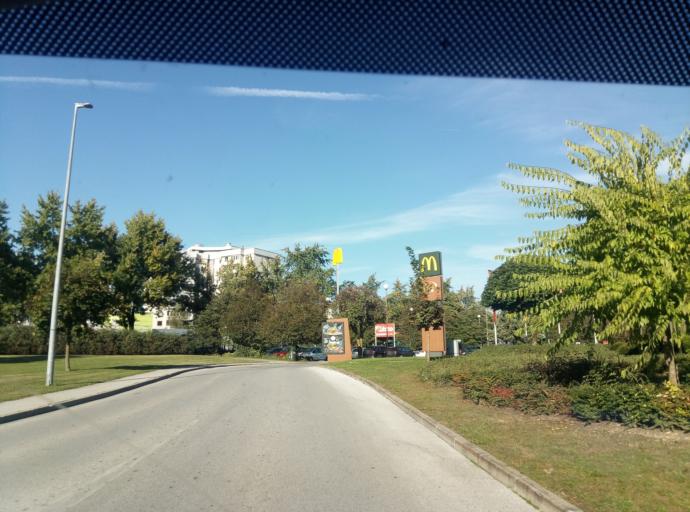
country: SI
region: Ljubljana
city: Ljubljana
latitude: 46.0691
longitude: 14.5466
